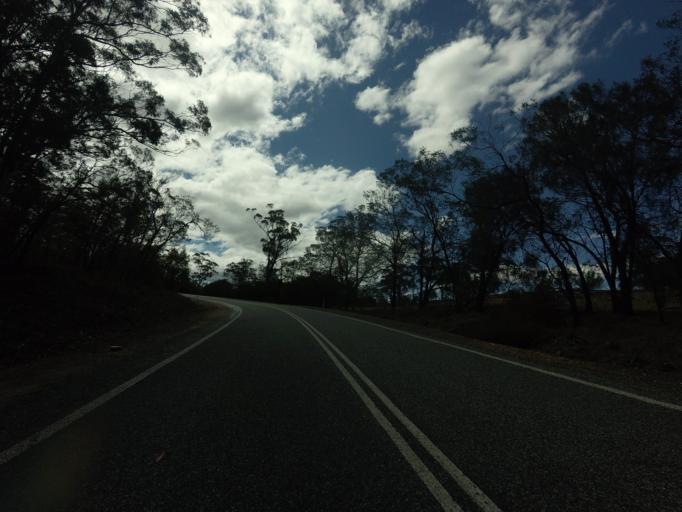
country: AU
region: Tasmania
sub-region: Break O'Day
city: St Helens
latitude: -42.0174
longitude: 148.0070
